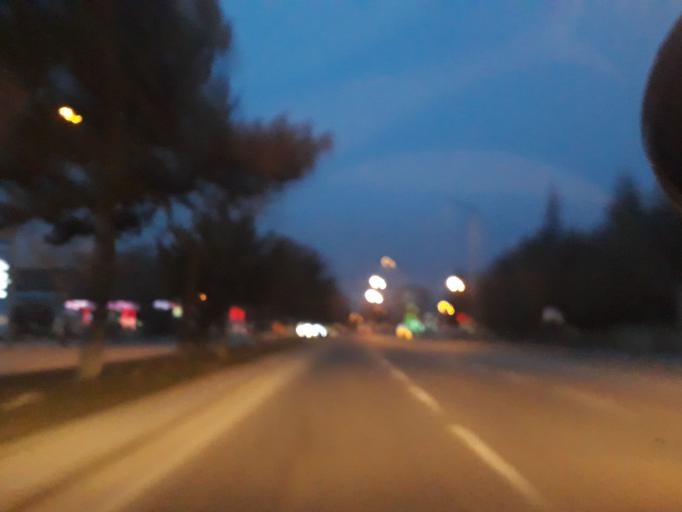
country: TR
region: Konya
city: Selcuklu
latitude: 37.8998
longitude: 32.5086
